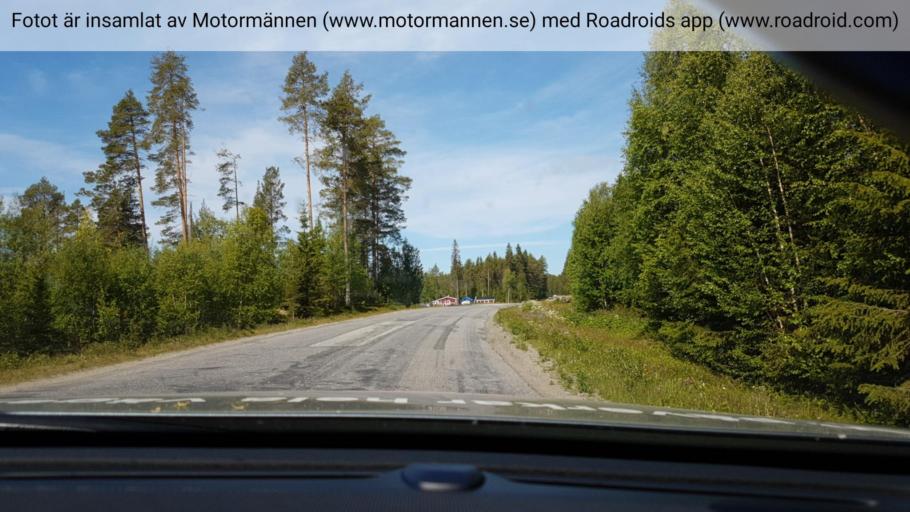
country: SE
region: Vaesterbotten
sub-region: Dorotea Kommun
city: Dorotea
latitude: 64.3583
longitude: 16.2131
